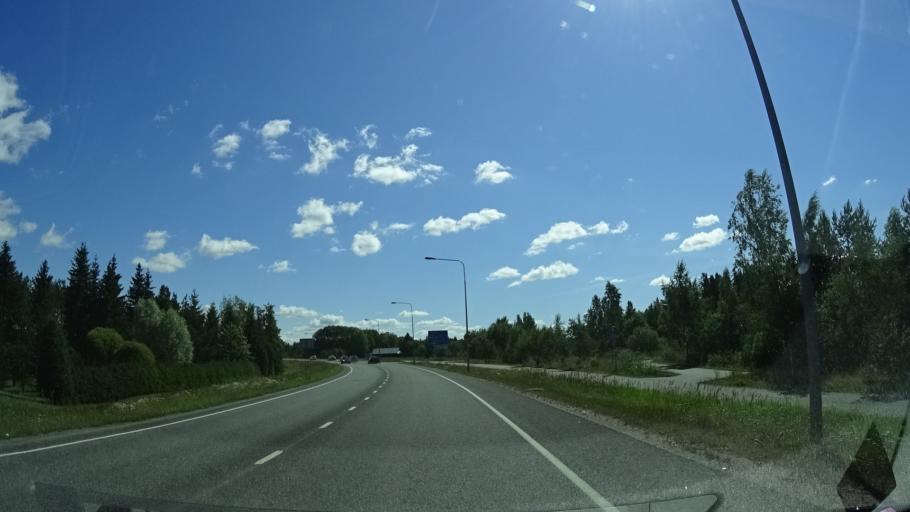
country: FI
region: Varsinais-Suomi
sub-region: Turku
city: Raisio
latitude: 60.5041
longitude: 22.1446
